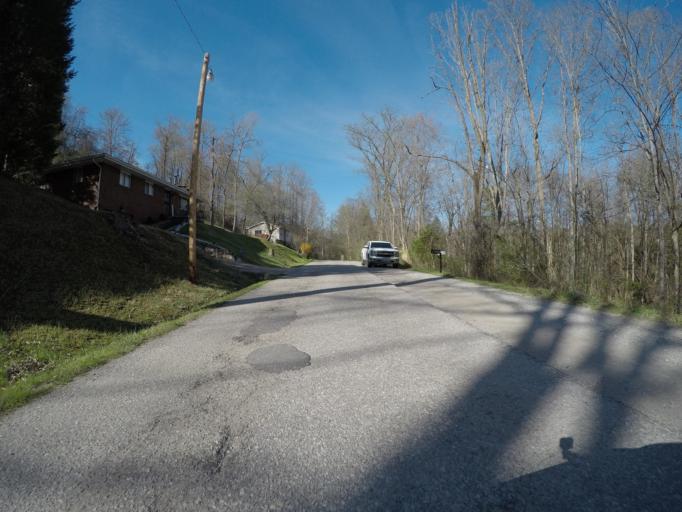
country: US
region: West Virginia
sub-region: Kanawha County
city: Charleston
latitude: 38.3843
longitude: -81.6039
